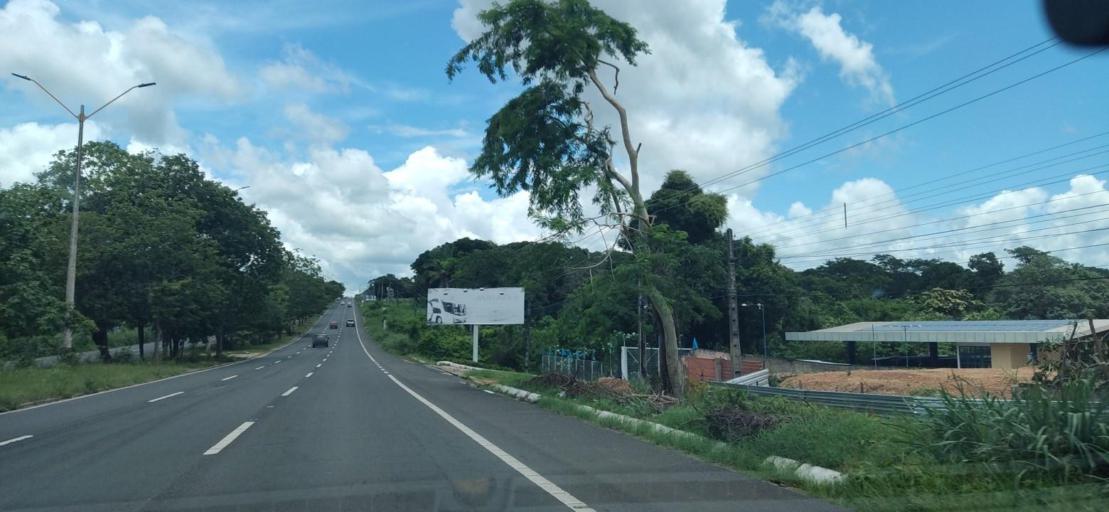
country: BR
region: Piaui
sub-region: Teresina
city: Teresina
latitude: -5.0803
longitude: -42.7572
